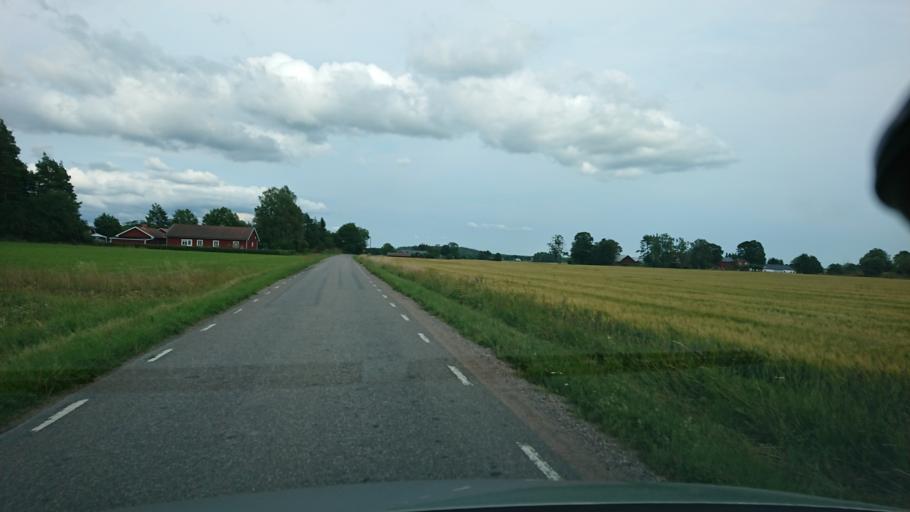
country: SE
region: Uppsala
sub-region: Osthammars Kommun
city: Bjorklinge
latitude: 59.9903
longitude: 17.5253
